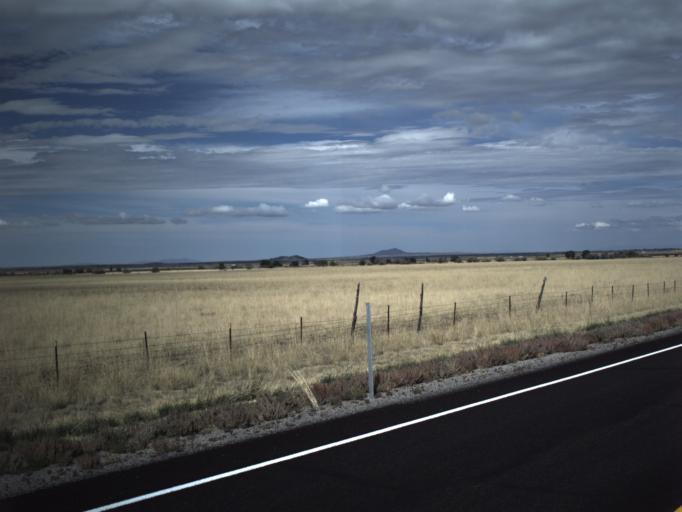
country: US
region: Utah
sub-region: Millard County
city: Fillmore
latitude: 38.8307
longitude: -112.4299
